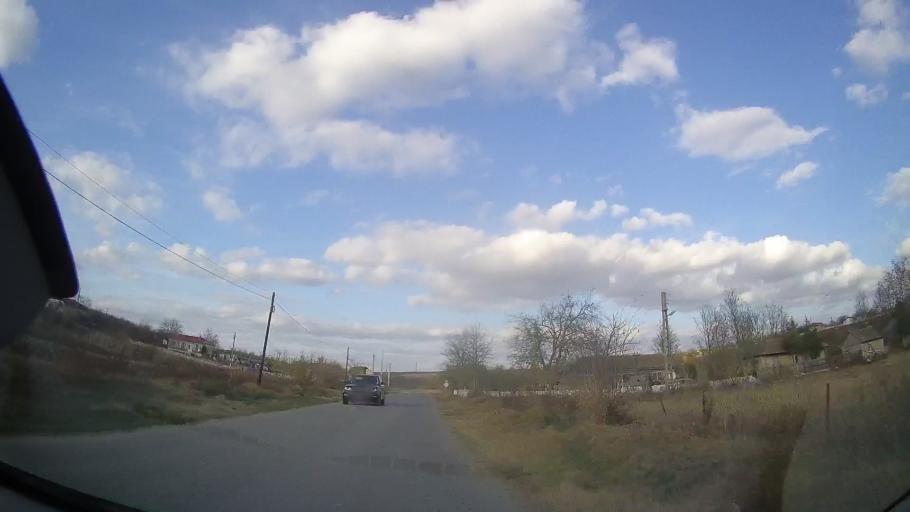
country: RO
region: Constanta
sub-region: Comuna Cerchezu
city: Cerchezu
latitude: 43.8255
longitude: 28.0976
